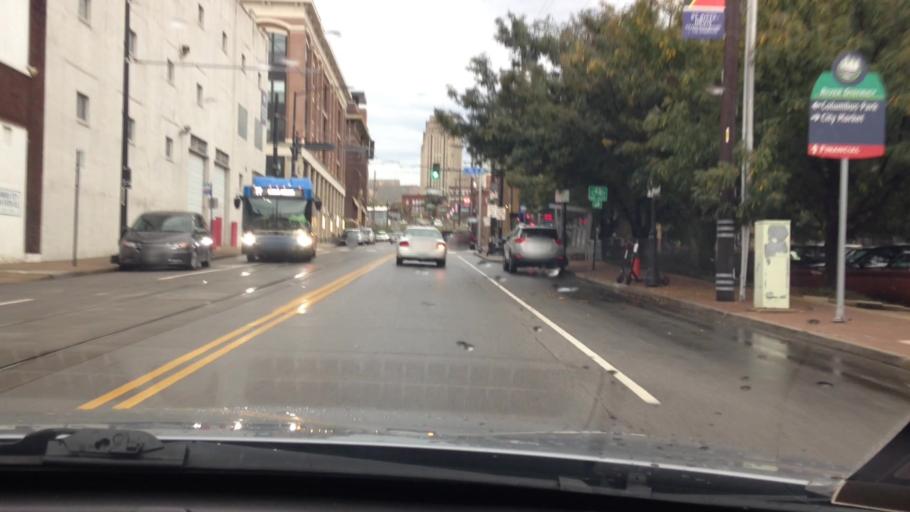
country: US
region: Missouri
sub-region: Jackson County
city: Kansas City
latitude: 39.1094
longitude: -94.5807
